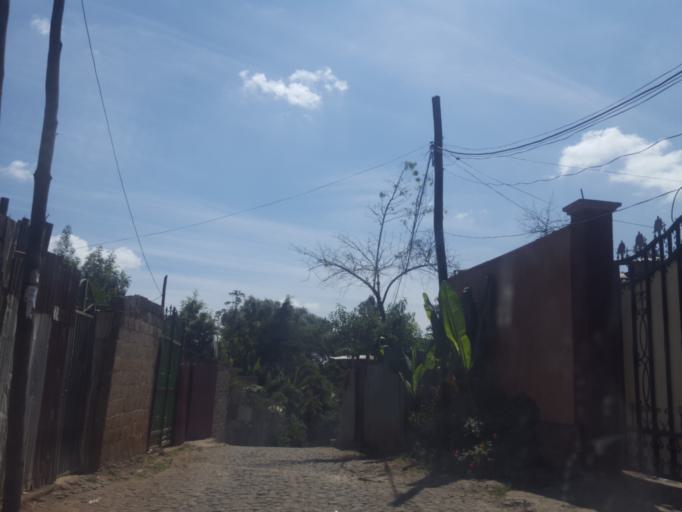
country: ET
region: Adis Abeba
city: Addis Ababa
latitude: 9.0523
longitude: 38.7305
